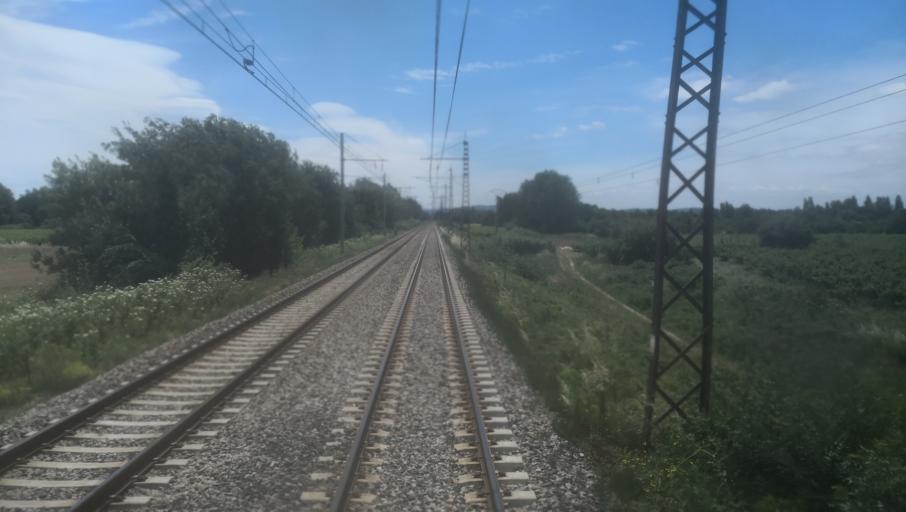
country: FR
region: Languedoc-Roussillon
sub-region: Departement de l'Aude
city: Coursan
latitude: 43.2126
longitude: 3.0283
